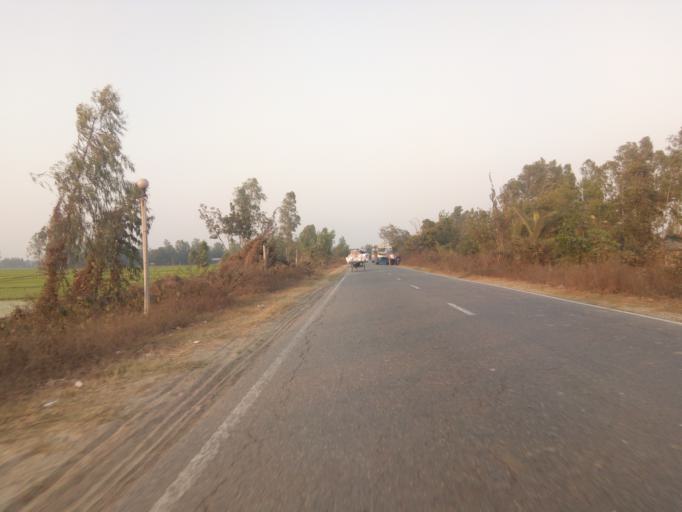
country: BD
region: Rajshahi
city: Bogra
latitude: 24.5990
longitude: 89.2388
